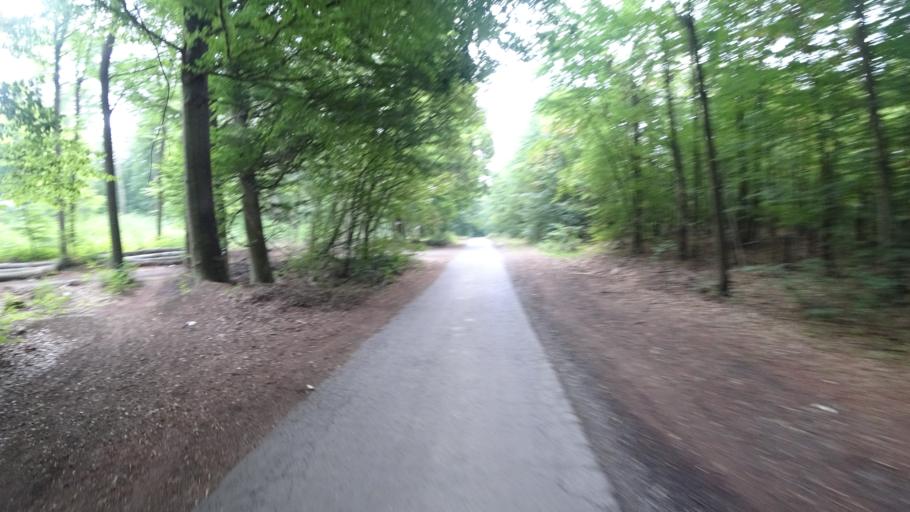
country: DE
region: Rheinland-Pfalz
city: Hohr-Grenzhausen
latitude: 50.4227
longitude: 7.6632
